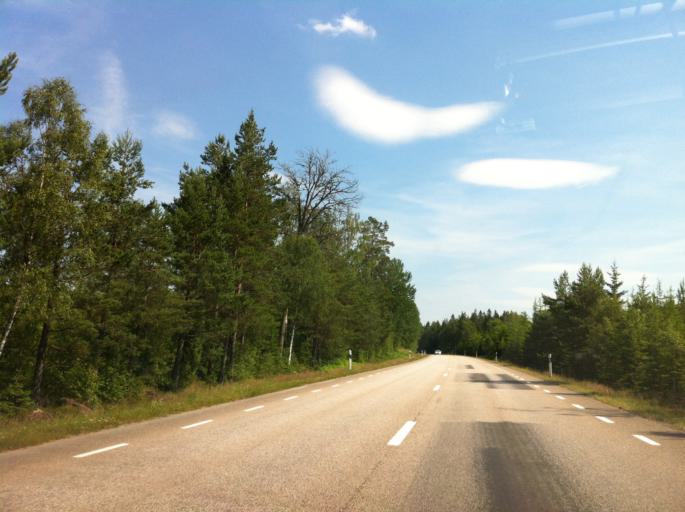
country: SE
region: Kalmar
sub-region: Nybro Kommun
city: Nybro
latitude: 56.8262
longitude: 15.7530
